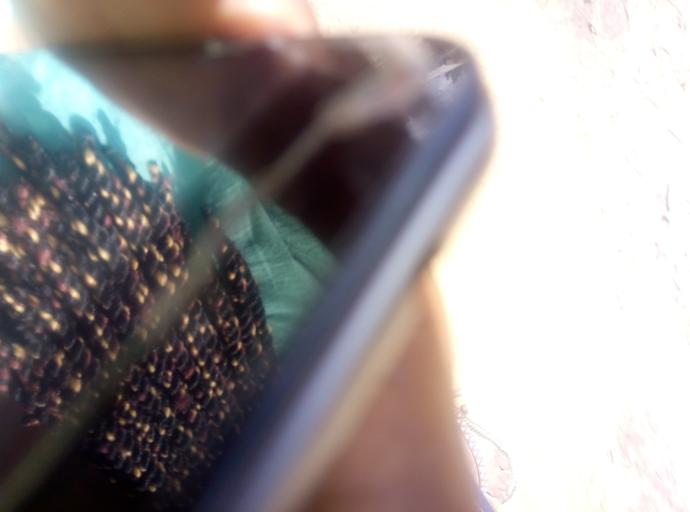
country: ML
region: Kayes
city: Yelimane
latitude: 15.1258
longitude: -10.7266
